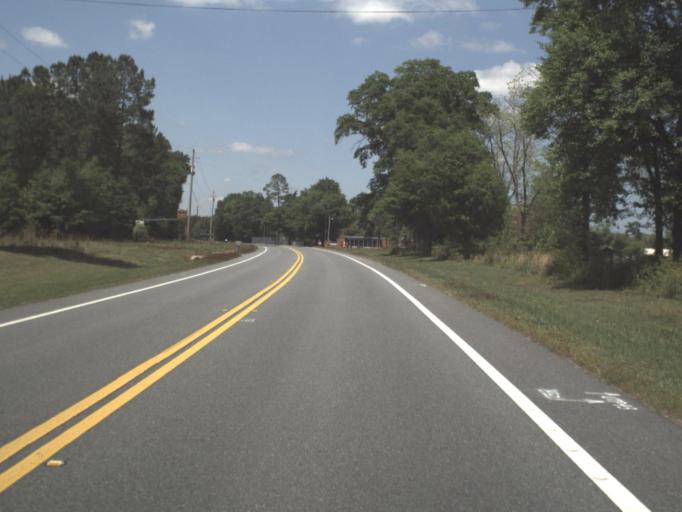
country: US
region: Alabama
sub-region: Escambia County
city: East Brewton
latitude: 30.9325
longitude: -87.0224
